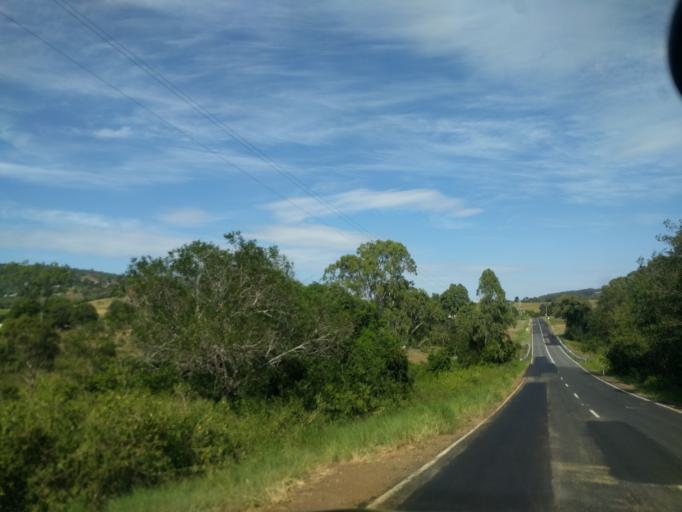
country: AU
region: Queensland
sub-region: Ipswich
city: Thagoona
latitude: -27.5933
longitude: 152.5565
